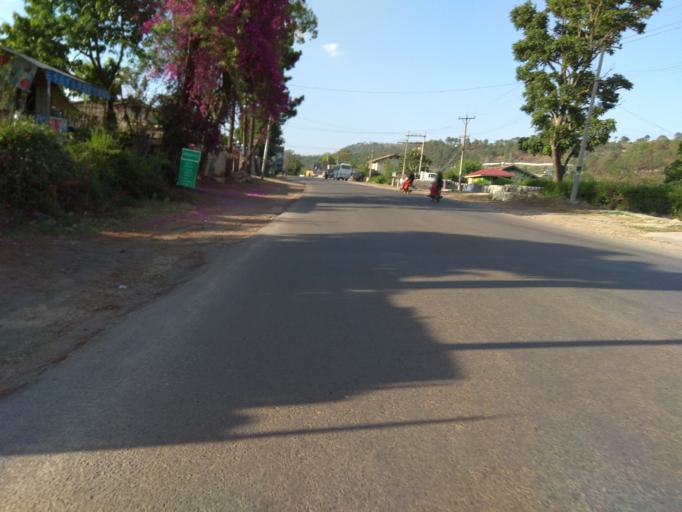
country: MM
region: Shan
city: Taunggyi
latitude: 20.6373
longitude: 96.5882
